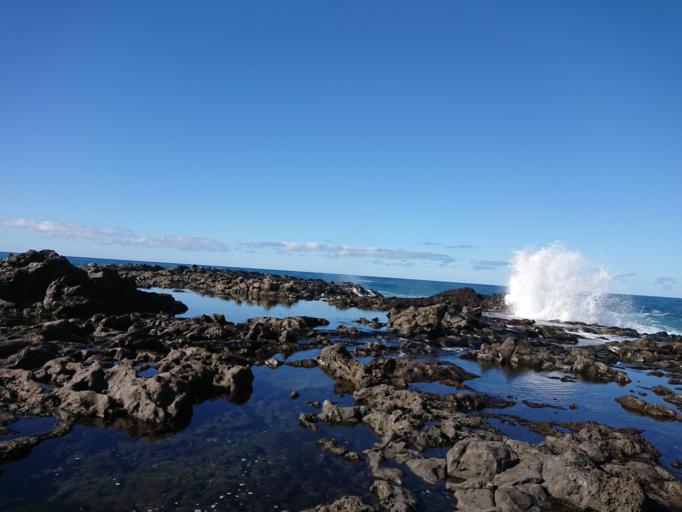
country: ES
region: Canary Islands
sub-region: Provincia de Las Palmas
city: Tinajo
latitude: 29.0835
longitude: -13.7253
